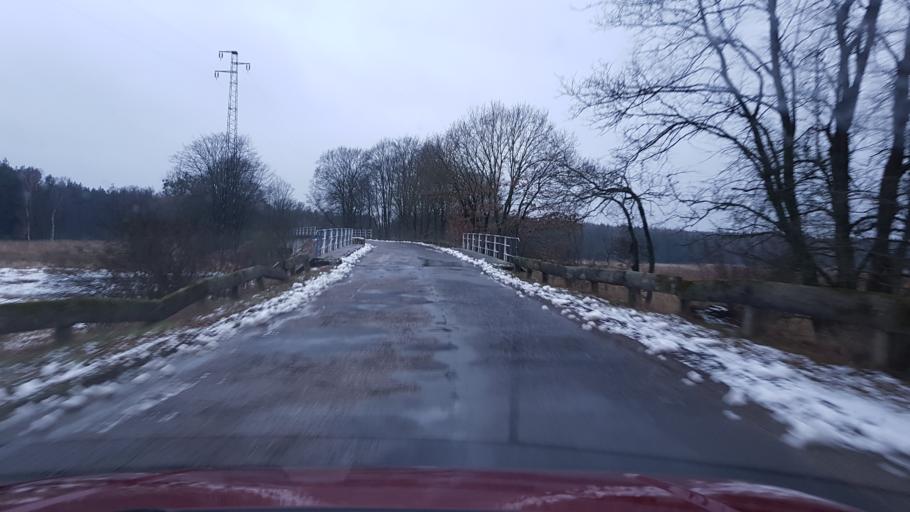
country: PL
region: West Pomeranian Voivodeship
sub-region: Powiat goleniowski
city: Goleniow
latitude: 53.4921
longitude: 14.8681
